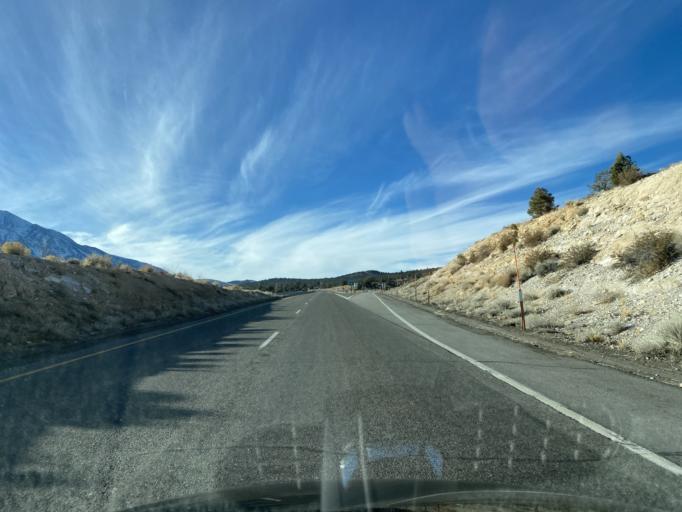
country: US
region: California
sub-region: Inyo County
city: West Bishop
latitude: 37.5165
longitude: -118.5883
